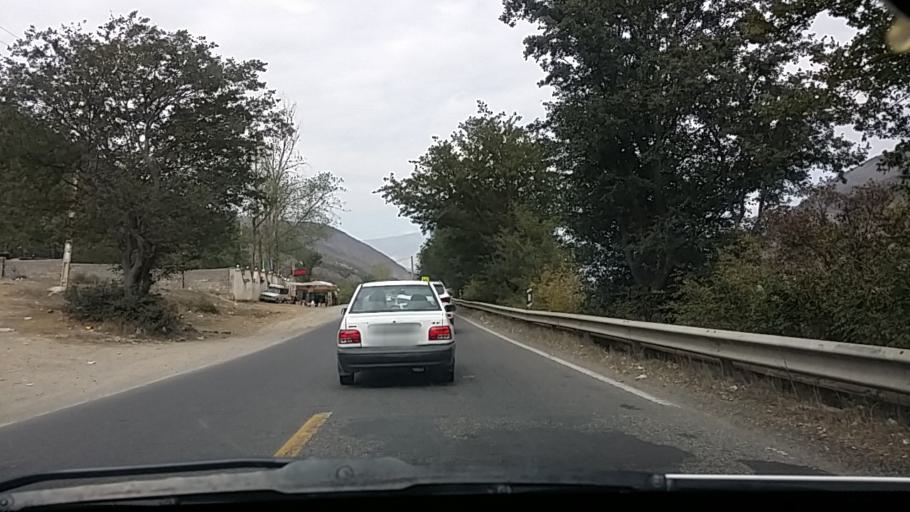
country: IR
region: Mazandaran
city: Chalus
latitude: 36.4096
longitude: 51.2786
